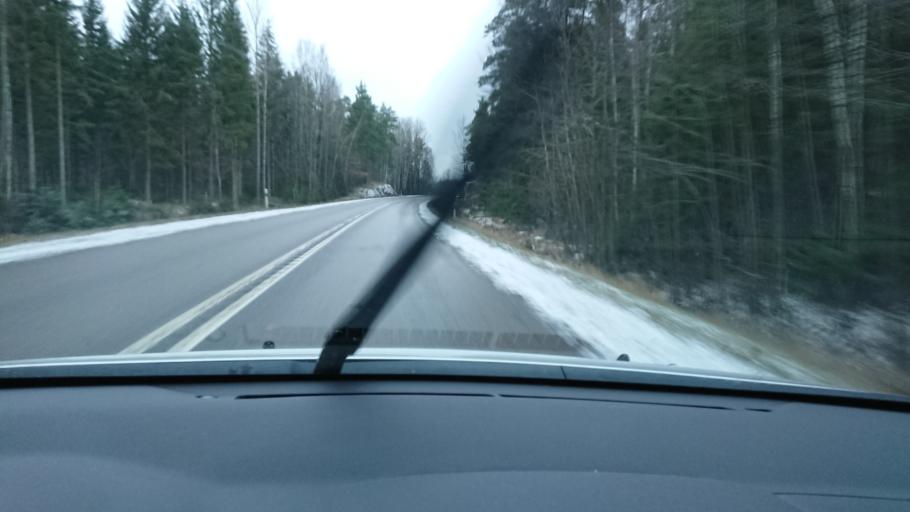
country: SE
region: Kalmar
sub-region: Hultsfreds Kommun
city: Hultsfred
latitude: 57.4948
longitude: 15.8215
